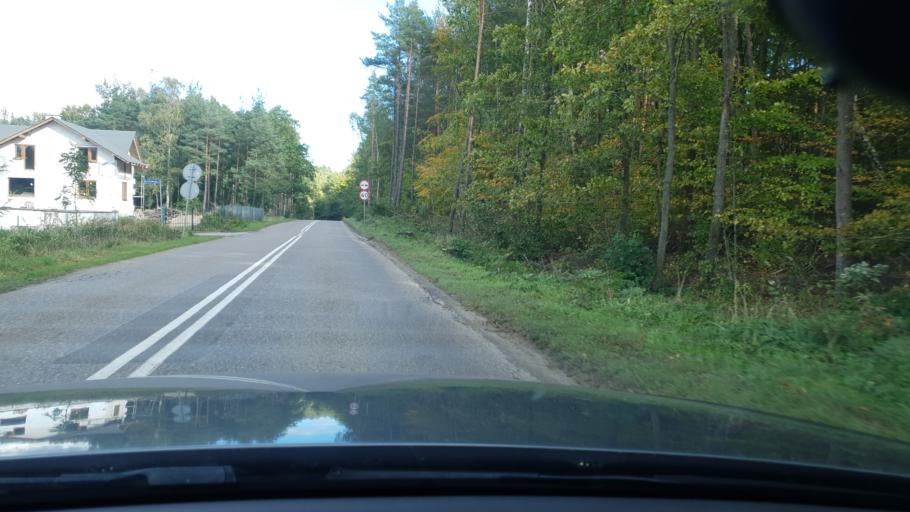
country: PL
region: Pomeranian Voivodeship
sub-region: Powiat wejherowski
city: Bojano
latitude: 54.5064
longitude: 18.3763
